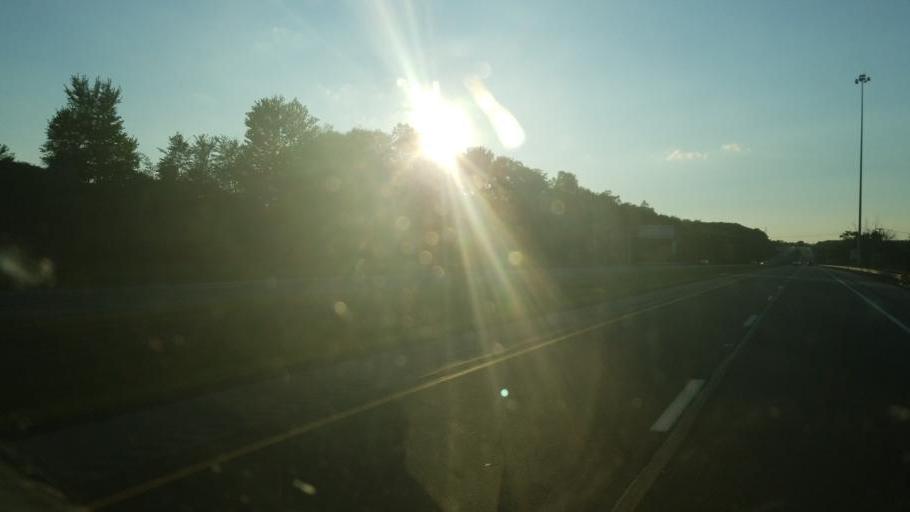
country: US
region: Ohio
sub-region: Mahoning County
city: New Middletown
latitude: 40.9276
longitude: -80.5631
